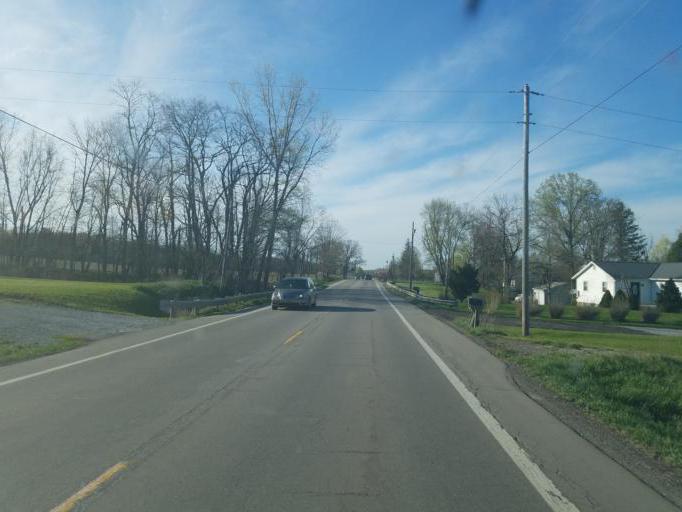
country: US
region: Ohio
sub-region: Ashland County
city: Ashland
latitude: 40.9352
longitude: -82.3534
